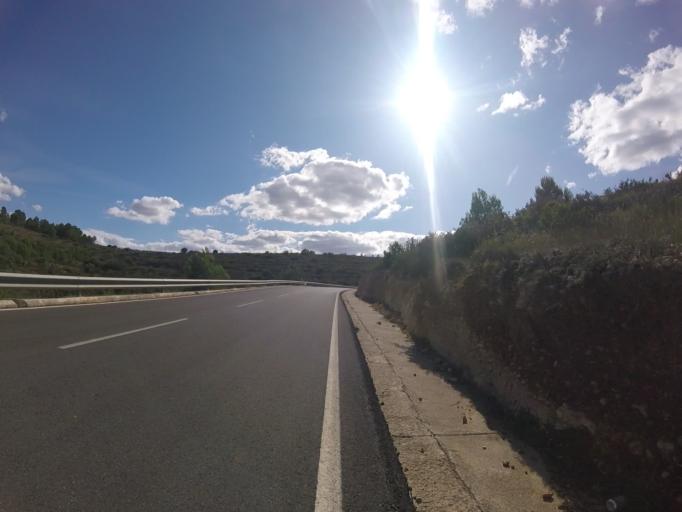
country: ES
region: Valencia
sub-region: Provincia de Castello
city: Cuevas de Vinroma
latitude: 40.3156
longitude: 0.1343
